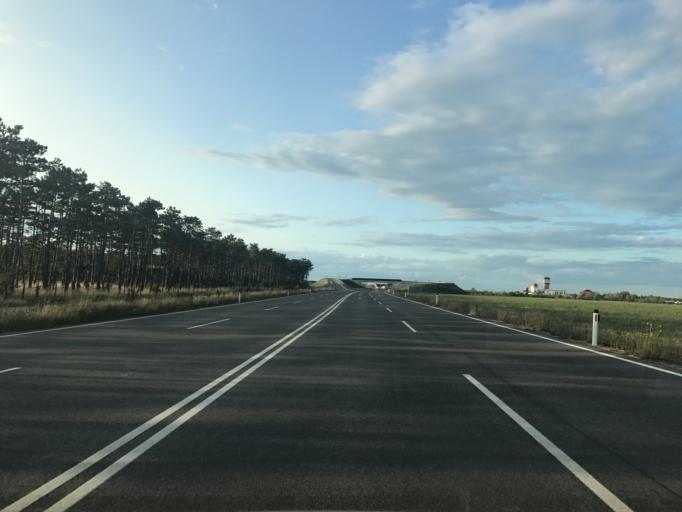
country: AT
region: Lower Austria
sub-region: Politischer Bezirk Wiener Neustadt
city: Lichtenworth
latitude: 47.8478
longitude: 16.2715
